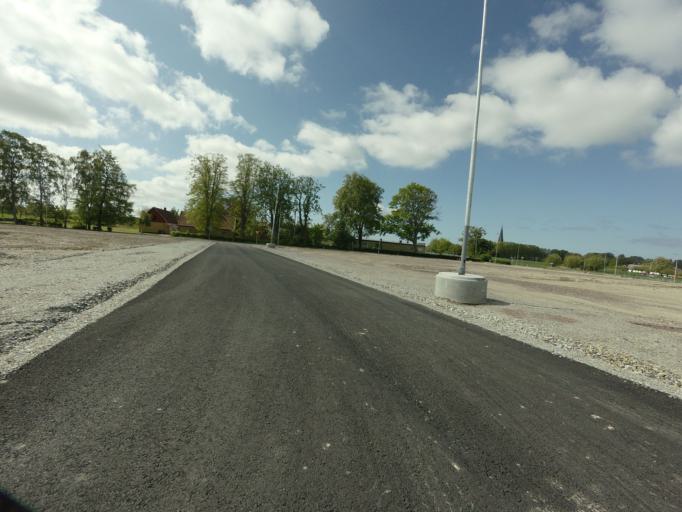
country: SE
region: Skane
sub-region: Malmo
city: Bunkeflostrand
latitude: 55.5582
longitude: 12.9703
